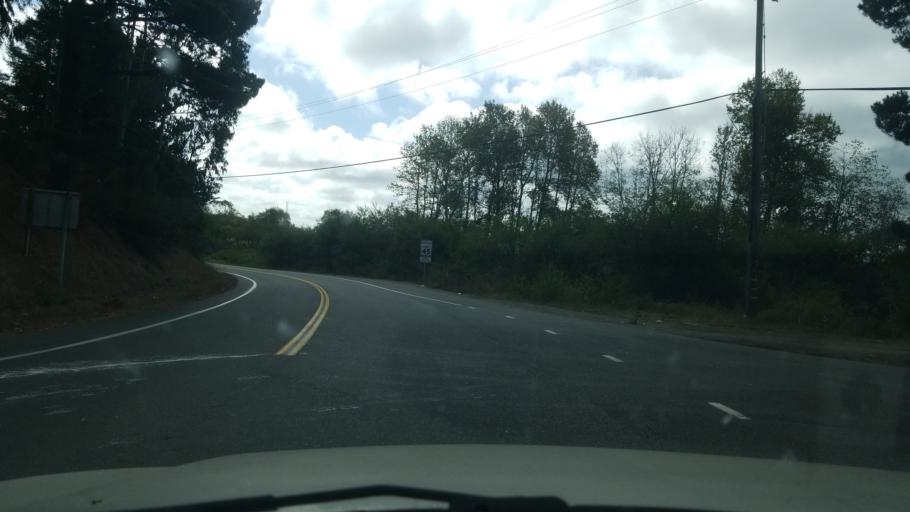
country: US
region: California
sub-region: Humboldt County
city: Fortuna
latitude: 40.6202
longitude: -124.2099
